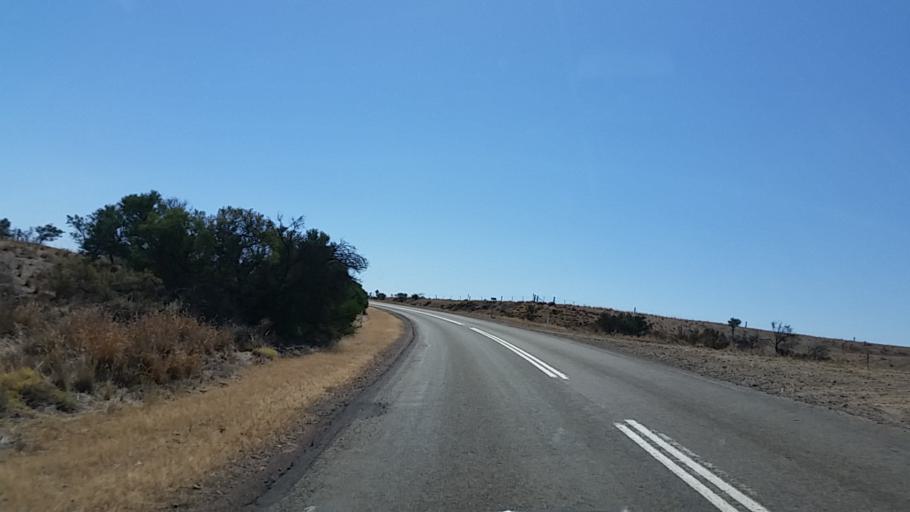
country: AU
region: South Australia
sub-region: Peterborough
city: Peterborough
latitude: -32.6377
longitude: 138.5983
